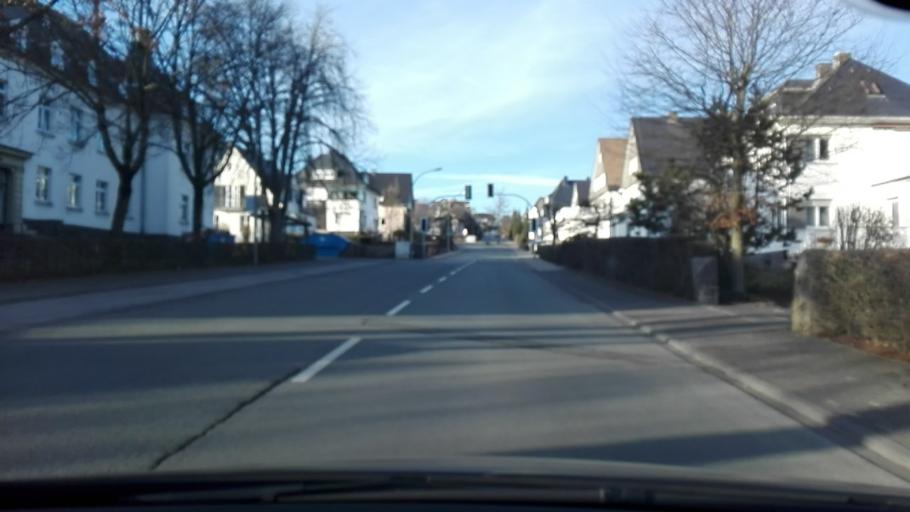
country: DE
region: North Rhine-Westphalia
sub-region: Regierungsbezirk Arnsberg
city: Schmallenberg
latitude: 51.1537
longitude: 8.2834
